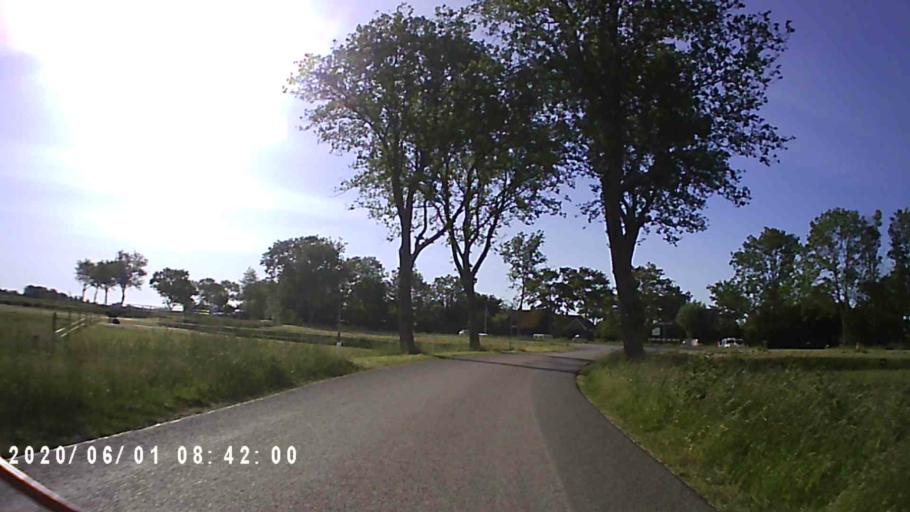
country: NL
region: Friesland
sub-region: Gemeente Ferwerderadiel
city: Burdaard
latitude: 53.2864
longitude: 5.8466
